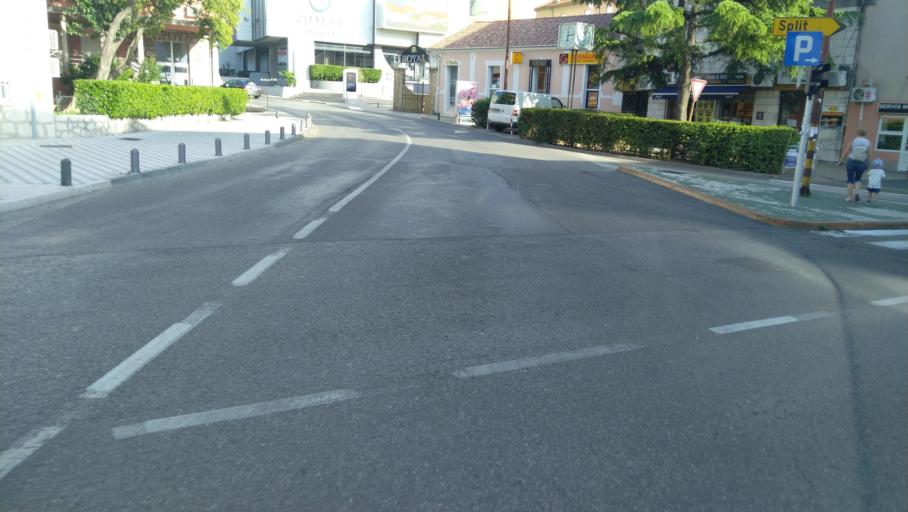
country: HR
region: Sibensko-Kniniska
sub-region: Grad Sibenik
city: Sibenik
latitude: 43.7321
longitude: 15.8968
